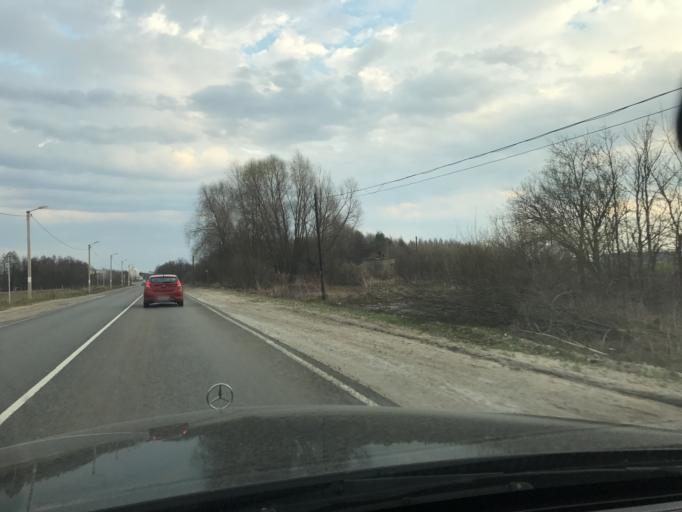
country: RU
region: Vladimir
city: Krasnaya Gorbatka
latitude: 55.6565
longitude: 41.8170
